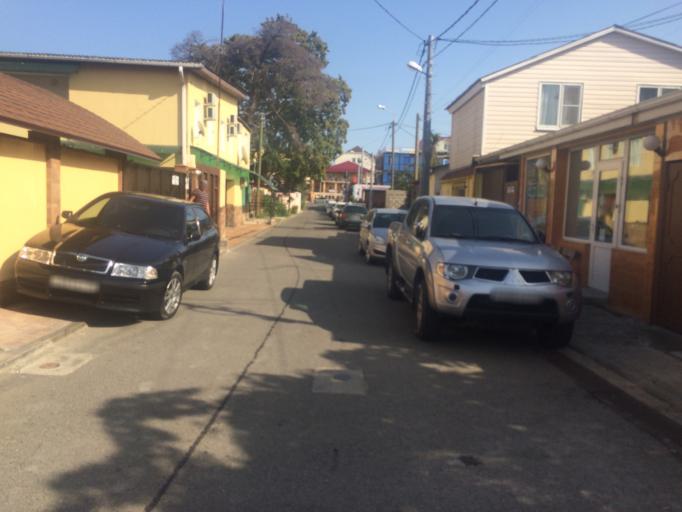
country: RU
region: Krasnodarskiy
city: Adler
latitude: 43.3931
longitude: 39.9857
